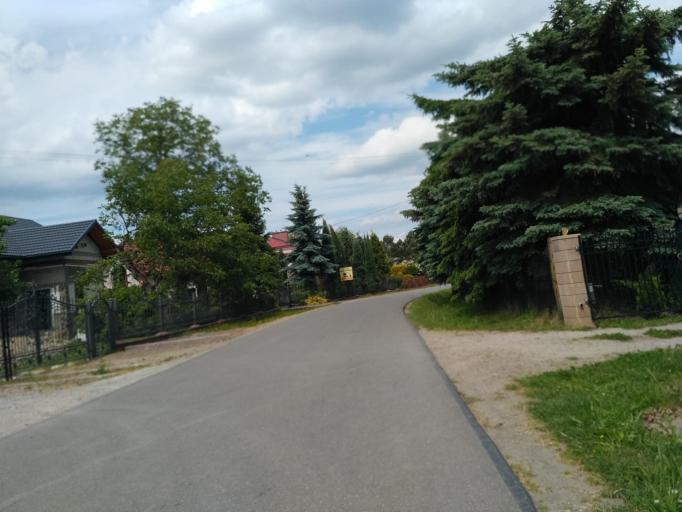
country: PL
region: Subcarpathian Voivodeship
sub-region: Powiat krosnienski
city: Chorkowka
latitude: 49.6806
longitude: 21.7048
